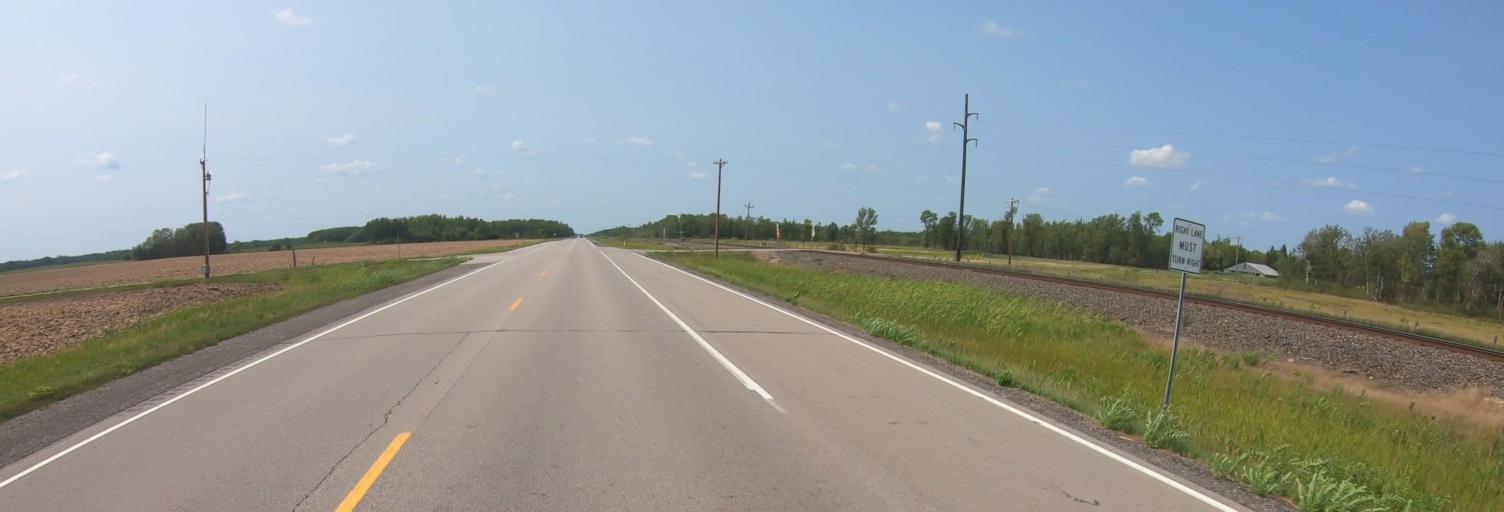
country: US
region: Minnesota
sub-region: Lake of the Woods County
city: Baudette
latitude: 48.7224
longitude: -94.7605
